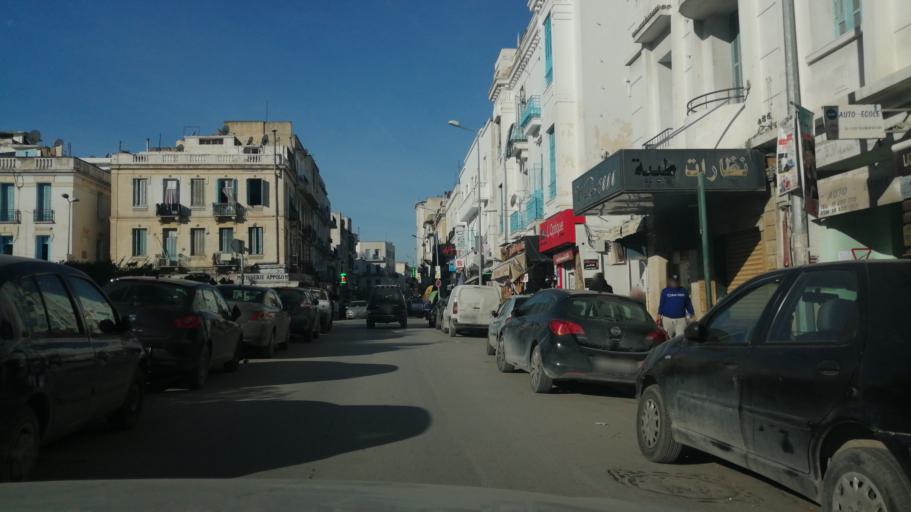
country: TN
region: Tunis
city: Tunis
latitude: 36.8058
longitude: 10.1768
